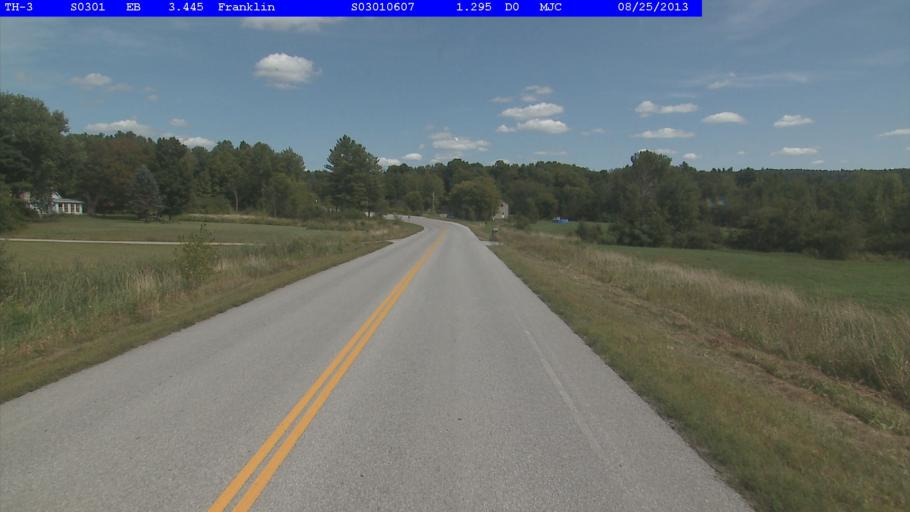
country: CA
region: Quebec
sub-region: Monteregie
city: Bedford
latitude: 44.9690
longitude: -72.9566
